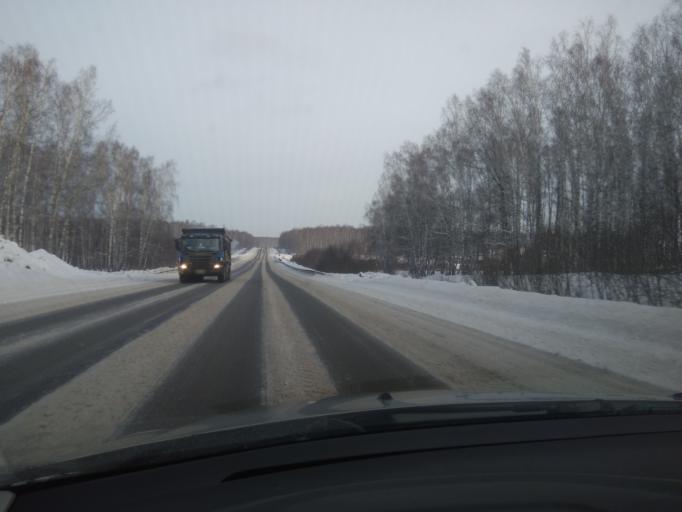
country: RU
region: Sverdlovsk
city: Bogdanovich
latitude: 56.7860
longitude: 61.9989
